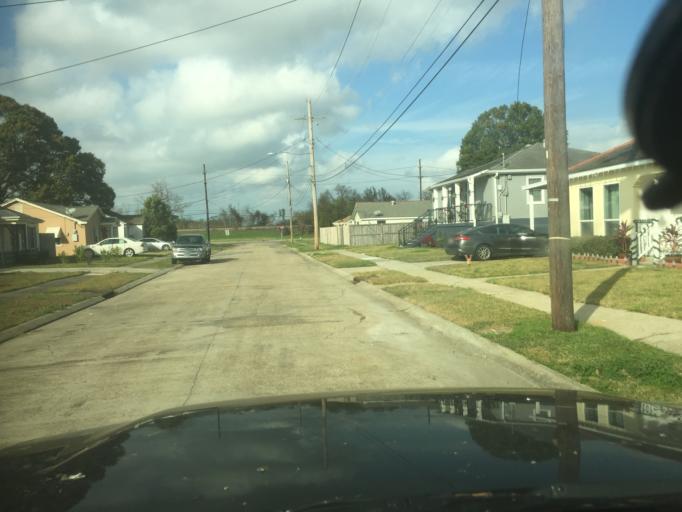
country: US
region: Louisiana
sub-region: Orleans Parish
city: New Orleans
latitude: 29.9909
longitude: -90.0802
